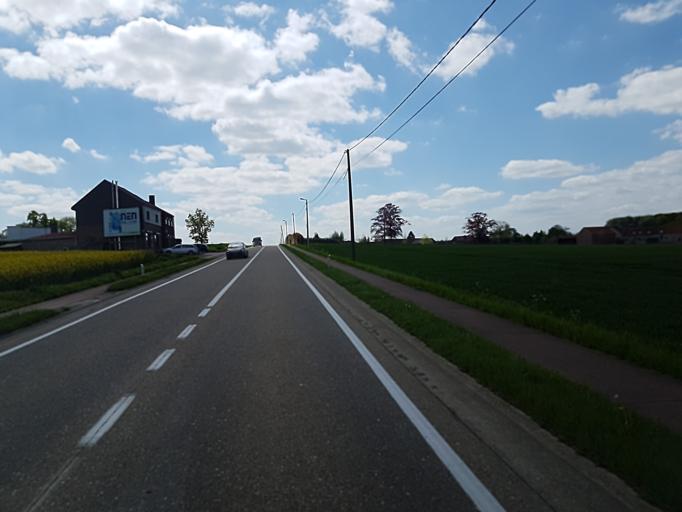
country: BE
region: Flanders
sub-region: Provincie Vlaams-Brabant
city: Bekkevoort
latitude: 50.9035
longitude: 4.9748
